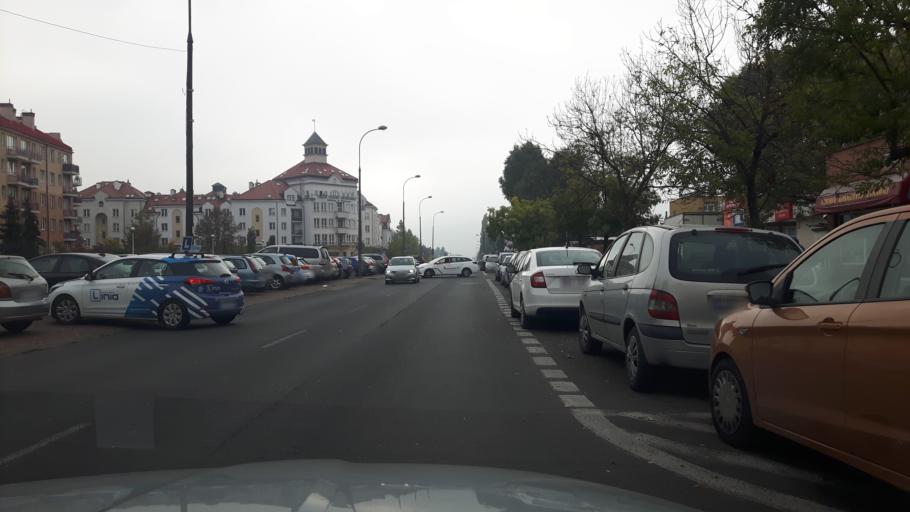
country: PL
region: Masovian Voivodeship
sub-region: Warszawa
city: Wlochy
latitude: 52.1929
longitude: 20.9675
